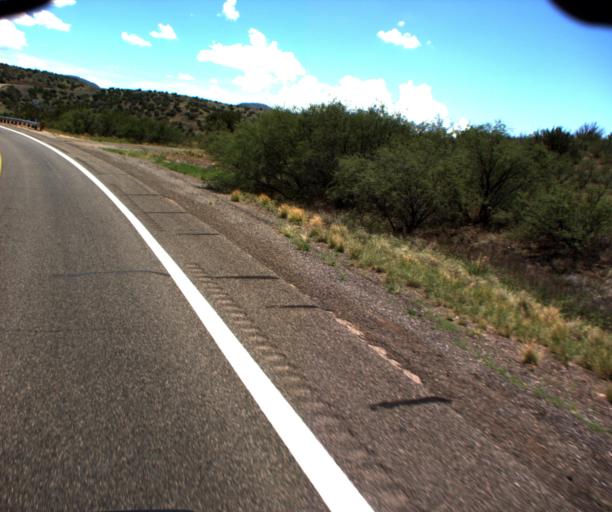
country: US
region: Arizona
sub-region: Yavapai County
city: Lake Montezuma
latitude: 34.5048
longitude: -111.7277
